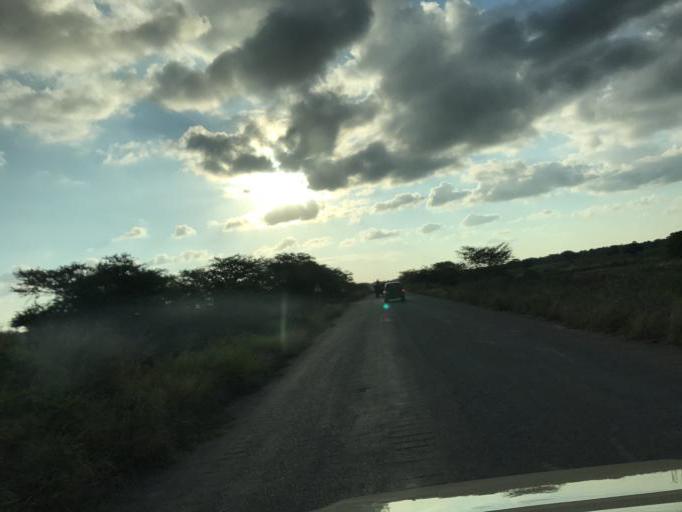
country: MZ
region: Gaza
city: Chibuto
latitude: -24.8203
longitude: 33.4494
